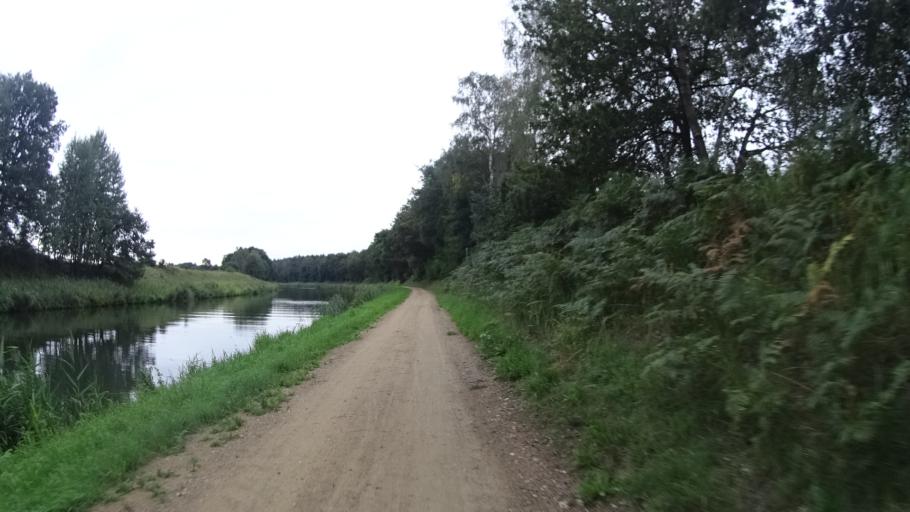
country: DE
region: Schleswig-Holstein
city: Grambek
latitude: 53.5885
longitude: 10.6659
